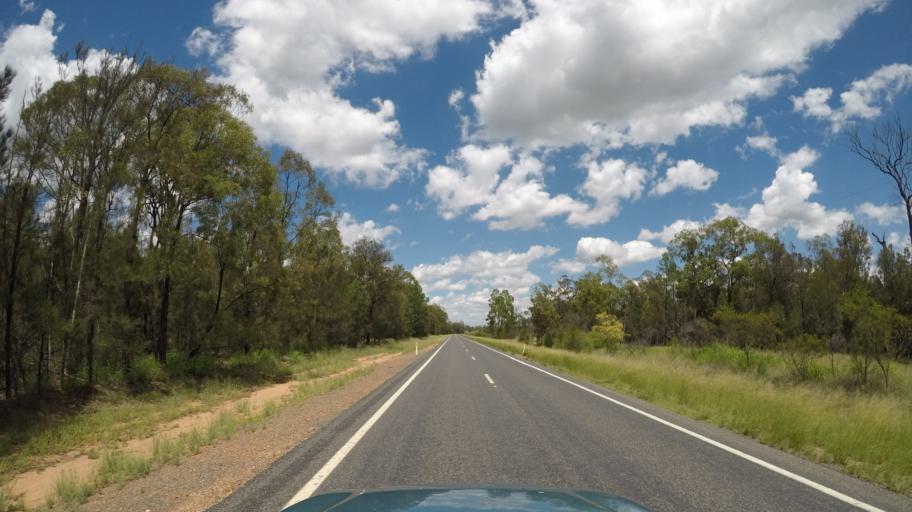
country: AU
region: Queensland
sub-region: Goondiwindi
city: Goondiwindi
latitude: -28.0050
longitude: 150.9296
